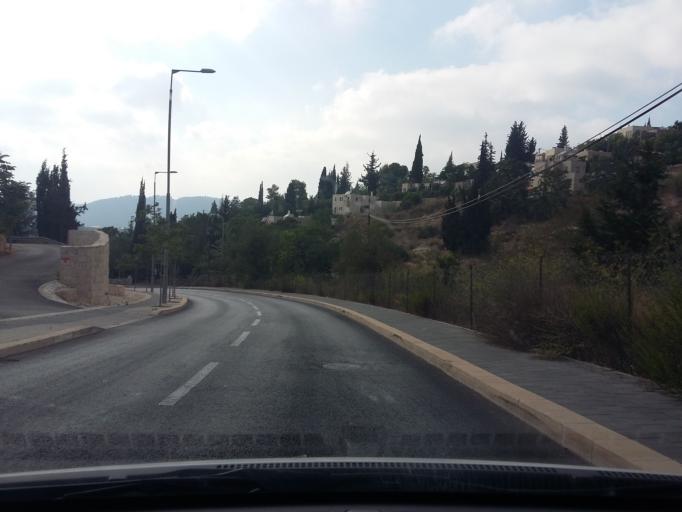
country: IL
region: Jerusalem
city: Jerusalem
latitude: 31.7656
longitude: 35.1687
